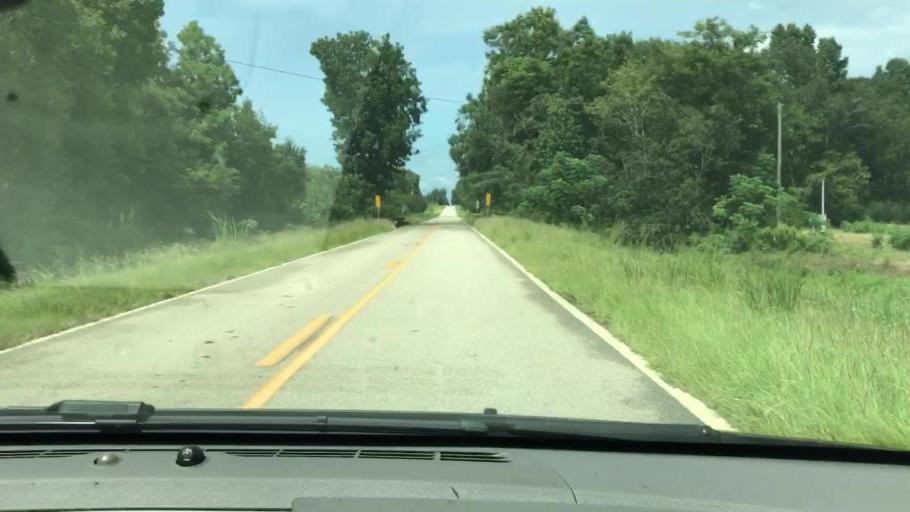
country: US
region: Georgia
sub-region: Seminole County
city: Donalsonville
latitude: 31.1229
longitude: -84.9956
